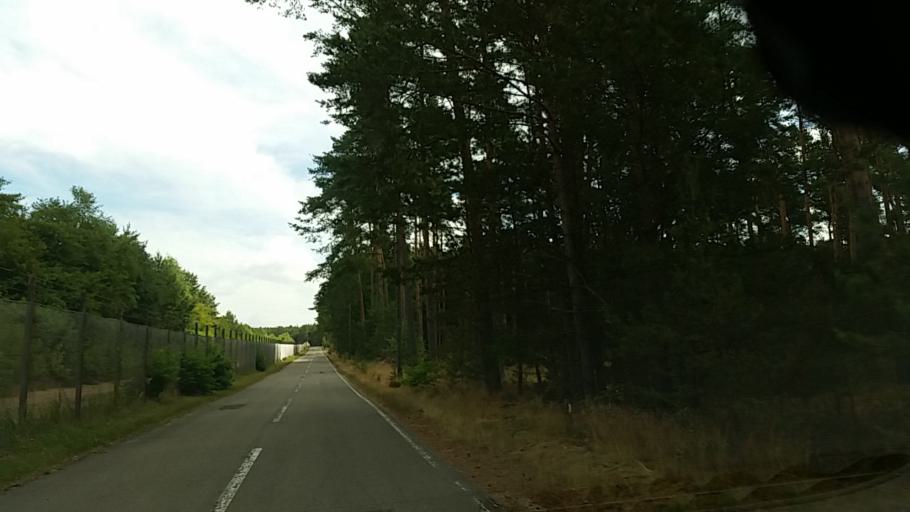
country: DE
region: Lower Saxony
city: Bergfeld
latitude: 52.5912
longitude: 10.7887
